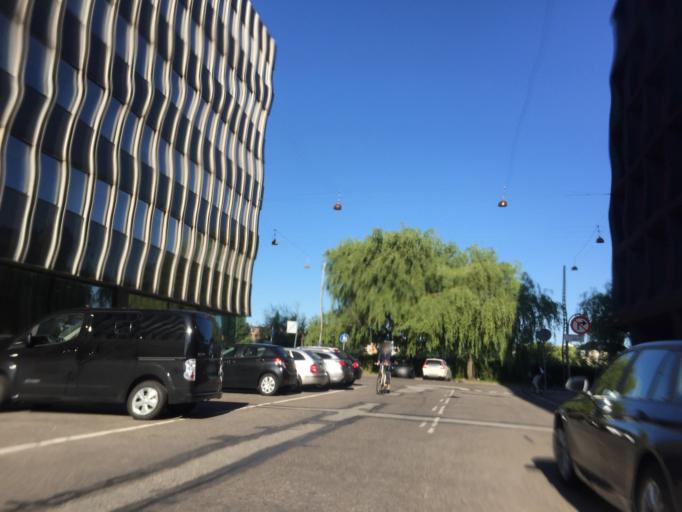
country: DK
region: Capital Region
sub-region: Kobenhavn
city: Copenhagen
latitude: 55.6762
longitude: 12.5599
